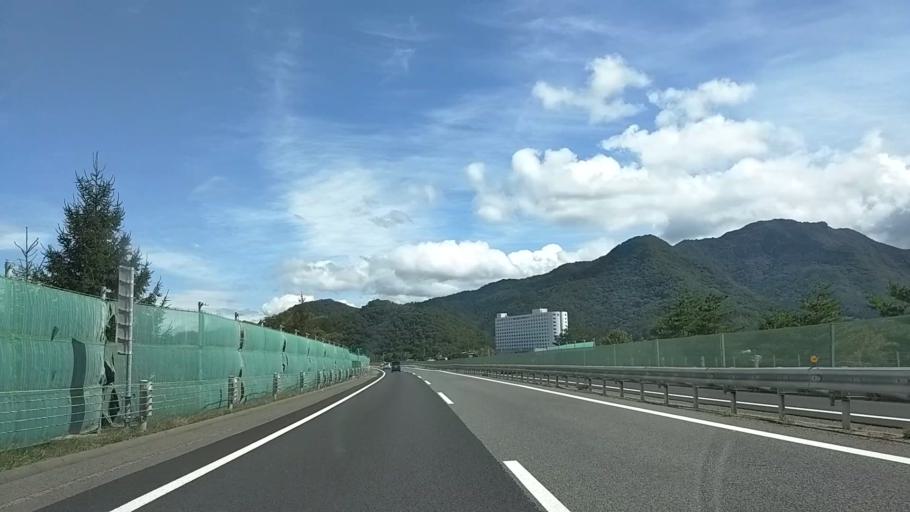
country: JP
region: Nagano
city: Nagano-shi
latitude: 36.5697
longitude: 138.1931
